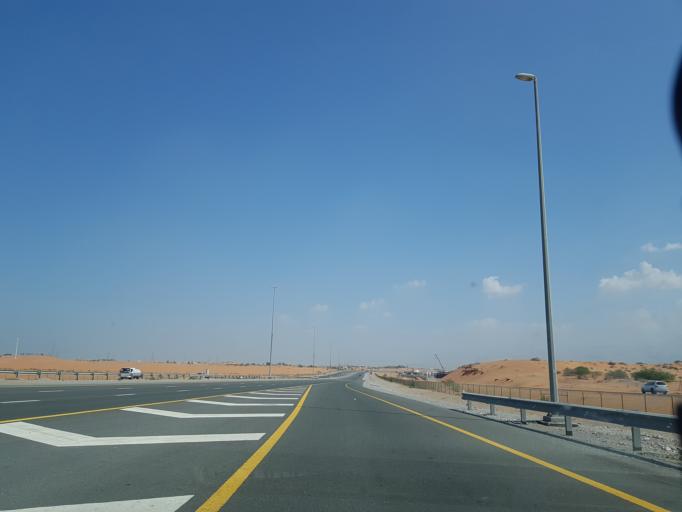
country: AE
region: Ra's al Khaymah
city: Ras al-Khaimah
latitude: 25.6970
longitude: 55.9282
